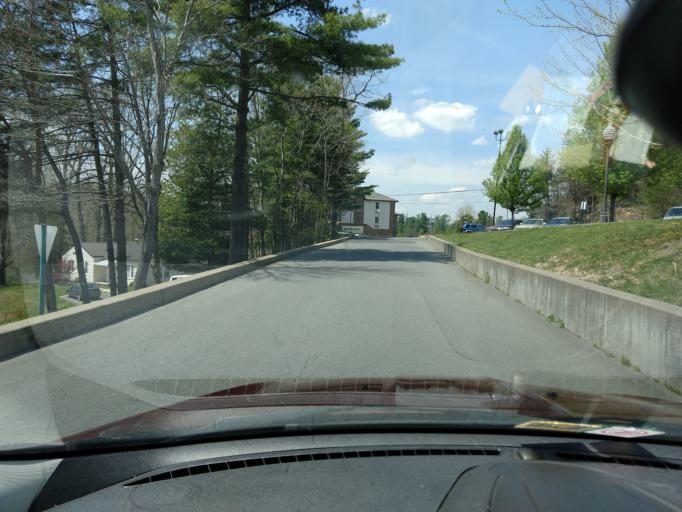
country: US
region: West Virginia
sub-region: Raleigh County
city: Bradley
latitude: 37.8532
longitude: -81.2015
